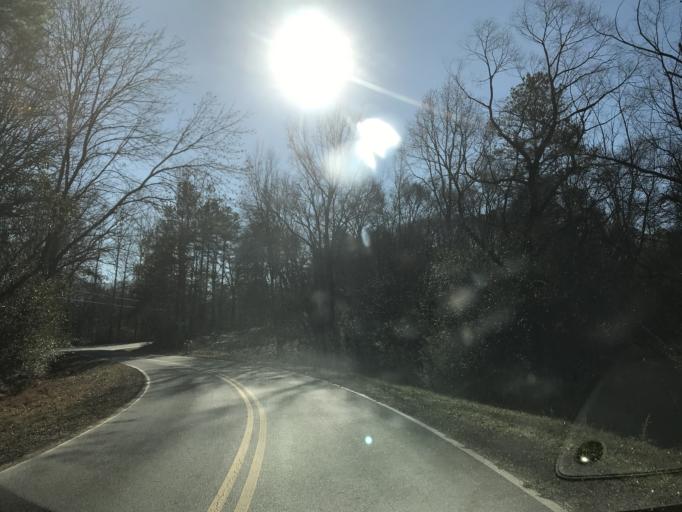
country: US
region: Georgia
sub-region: Paulding County
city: Dallas
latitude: 33.9958
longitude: -84.8942
